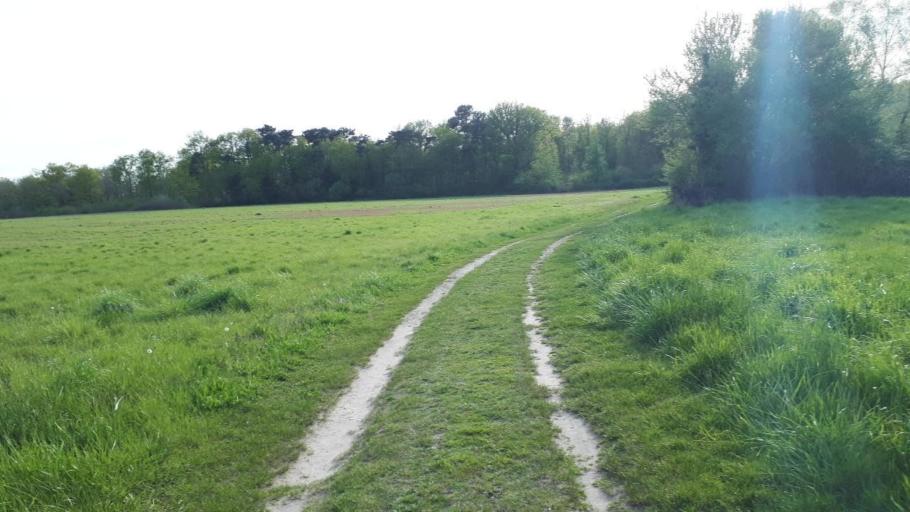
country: FR
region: Centre
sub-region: Departement du Loir-et-Cher
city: Saint-Romain-sur-Cher
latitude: 47.3614
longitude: 1.4025
